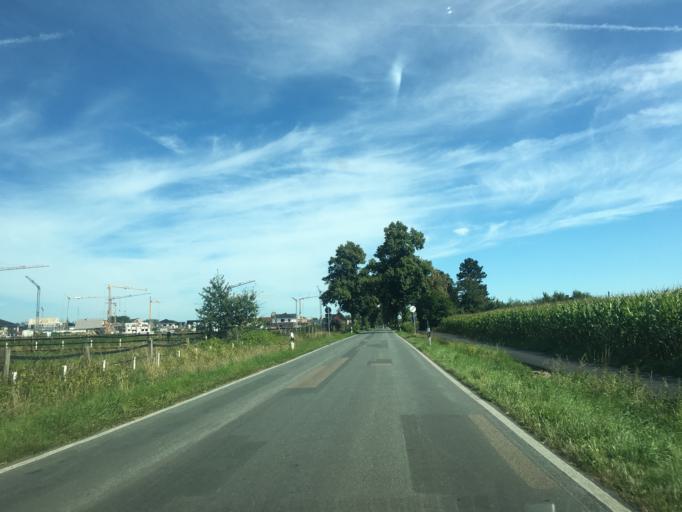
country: DE
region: North Rhine-Westphalia
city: Olfen
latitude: 51.7161
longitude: 7.3606
